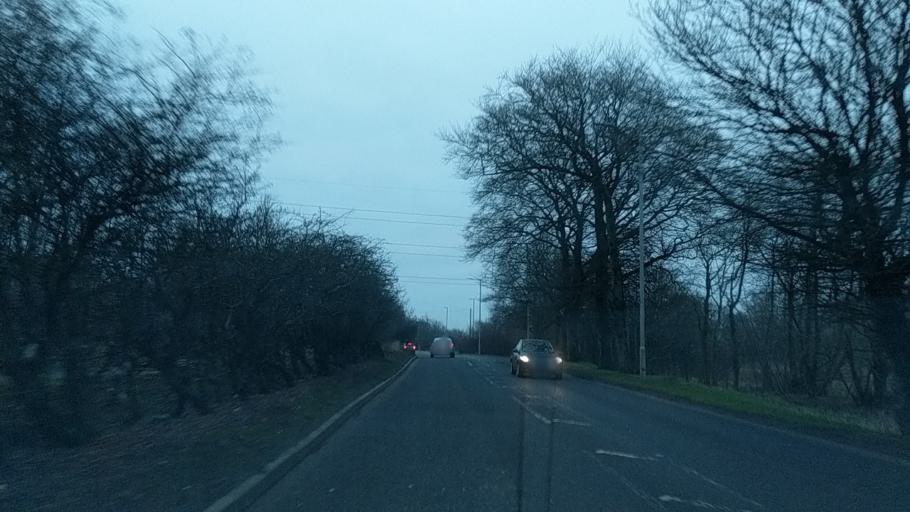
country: GB
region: Scotland
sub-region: South Lanarkshire
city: East Kilbride
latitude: 55.7439
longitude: -4.1579
